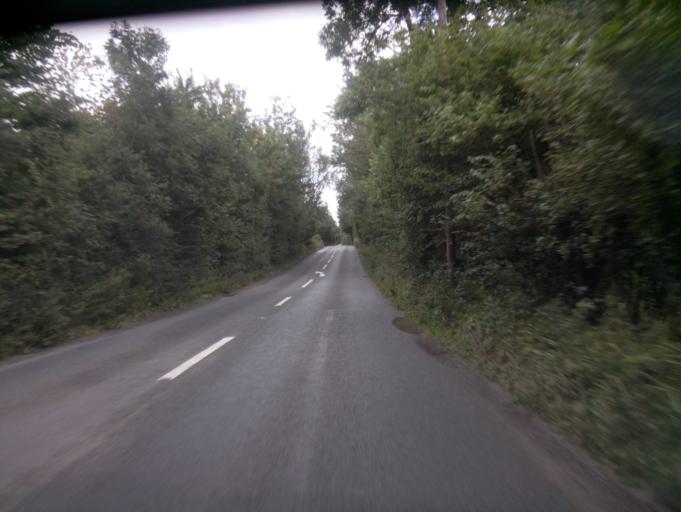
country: GB
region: England
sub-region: Devon
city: Modbury
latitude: 50.3374
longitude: -3.8564
